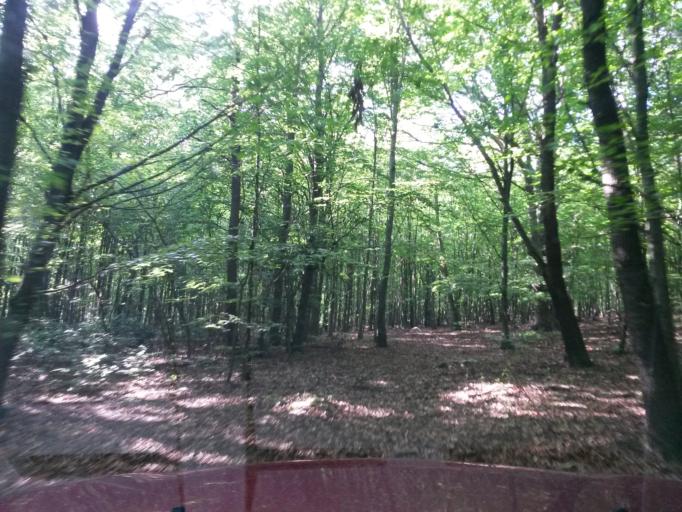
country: SK
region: Kosicky
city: Moldava nad Bodvou
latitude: 48.7272
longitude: 21.0819
